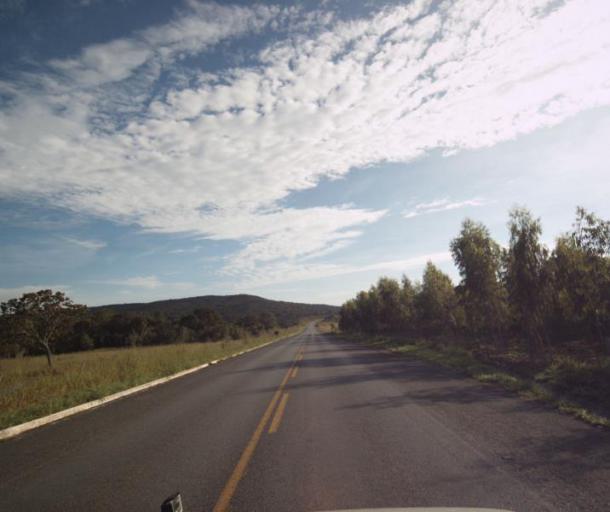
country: BR
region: Goias
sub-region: Pirenopolis
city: Pirenopolis
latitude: -15.6590
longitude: -48.6844
